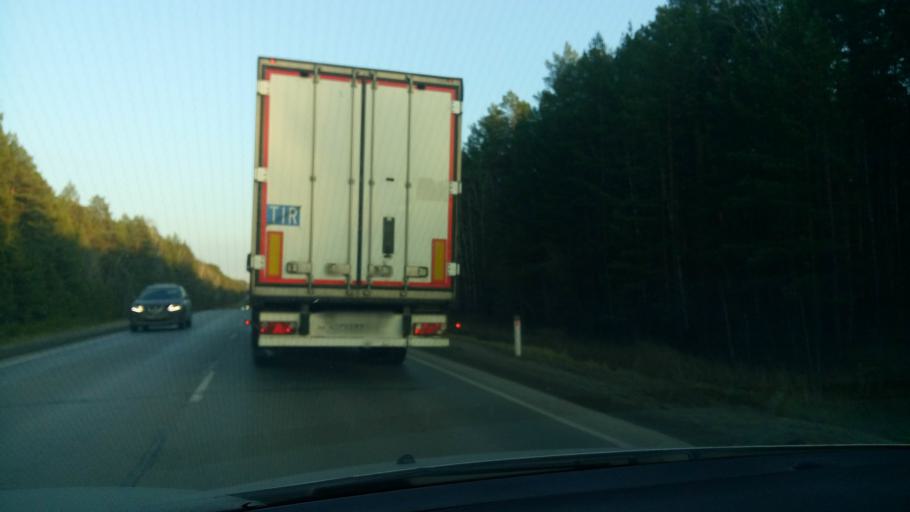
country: RU
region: Sverdlovsk
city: Yelanskiy
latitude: 56.7576
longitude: 62.2970
